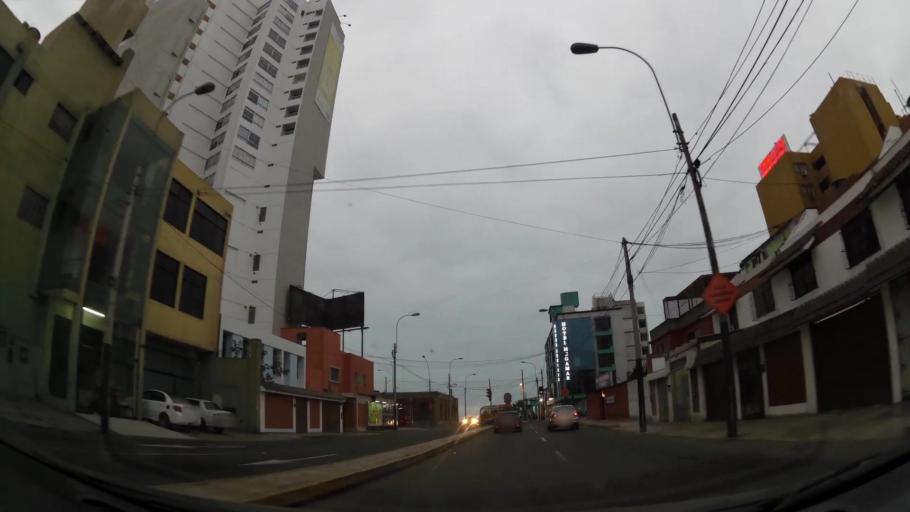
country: PE
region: Lima
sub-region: Lima
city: San Isidro
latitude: -12.0965
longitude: -77.0722
